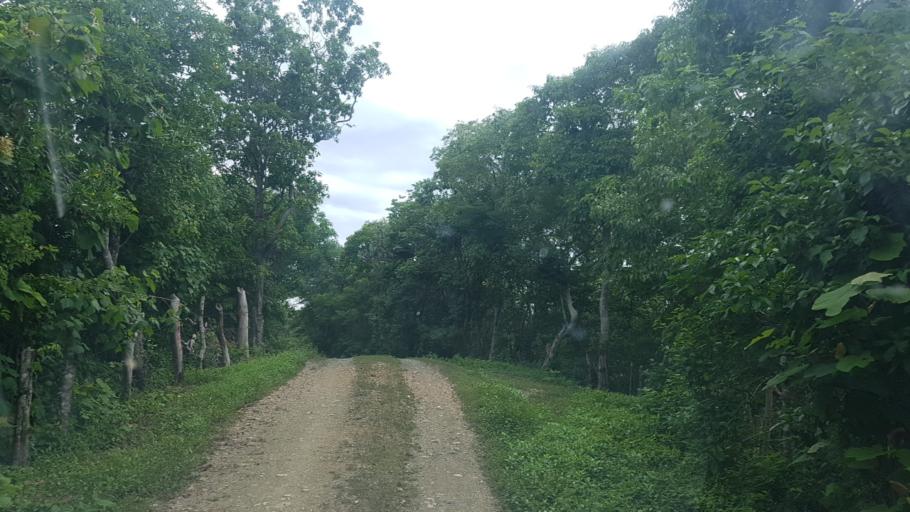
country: NI
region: Nueva Segovia
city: Ciudad Antigua
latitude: 13.5993
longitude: -86.3647
